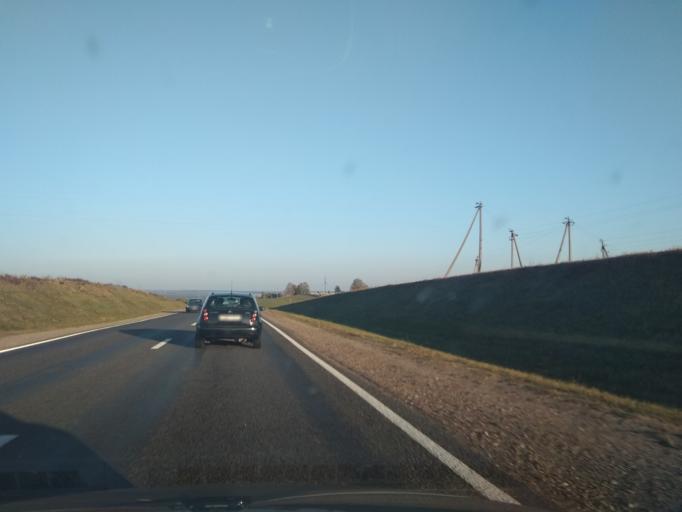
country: BY
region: Grodnenskaya
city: Zel'va
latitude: 53.1419
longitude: 24.7913
